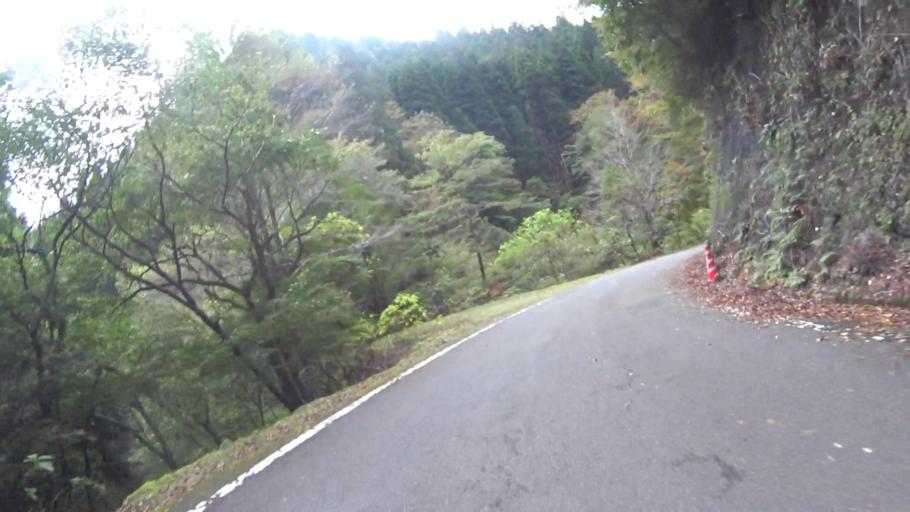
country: JP
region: Fukui
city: Obama
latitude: 35.2760
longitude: 135.7181
